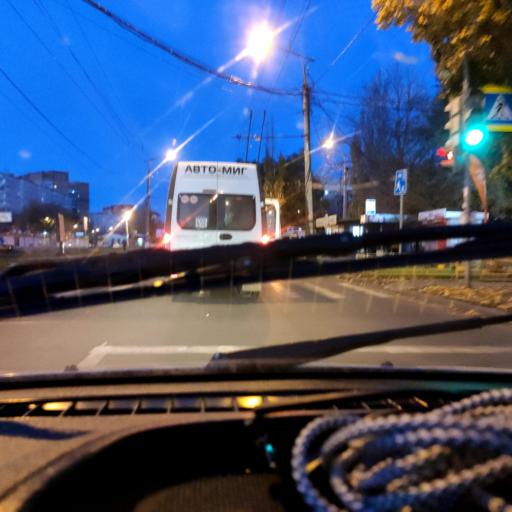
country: RU
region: Samara
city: Tol'yatti
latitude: 53.5115
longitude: 49.4448
